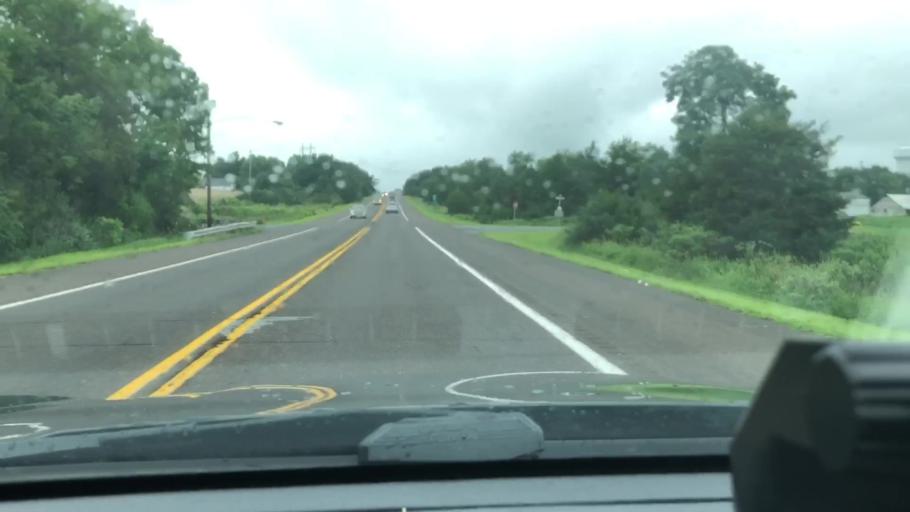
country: US
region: Pennsylvania
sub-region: Bucks County
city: Spinnerstown
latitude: 40.4268
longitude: -75.4382
